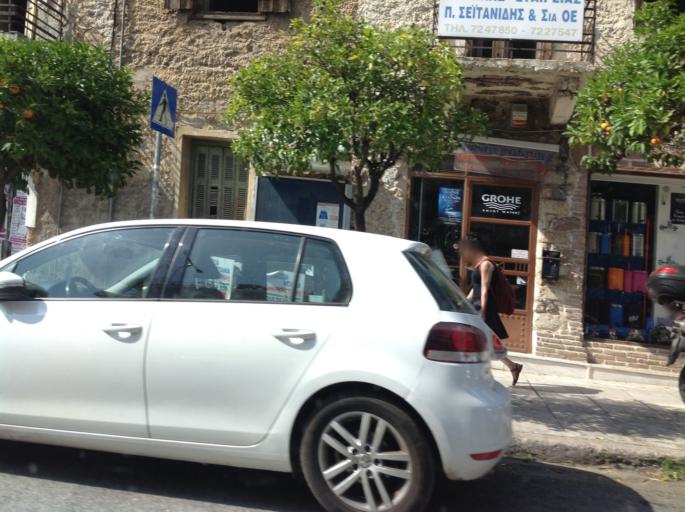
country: GR
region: Attica
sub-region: Nomarchia Athinas
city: Kaisariani
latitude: 37.9685
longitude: 23.7583
